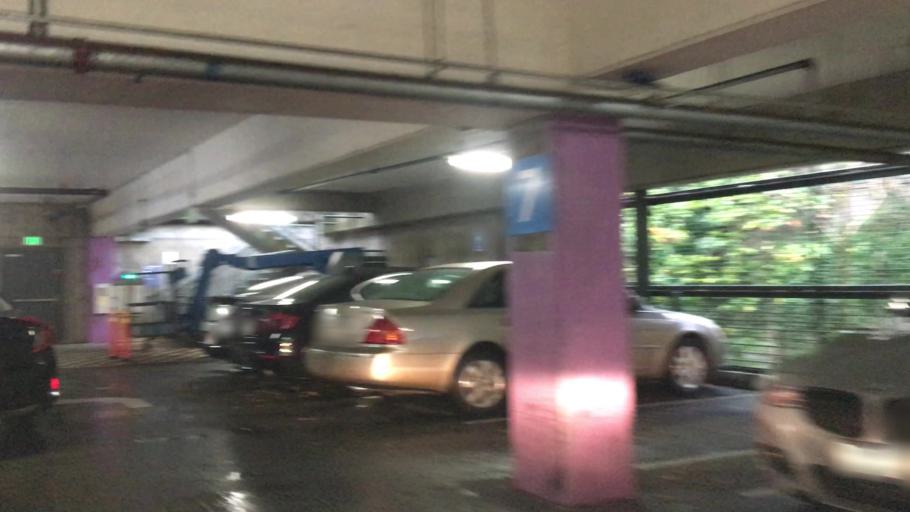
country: US
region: Washington
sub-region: King County
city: Yarrow Point
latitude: 47.6617
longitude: -122.2802
